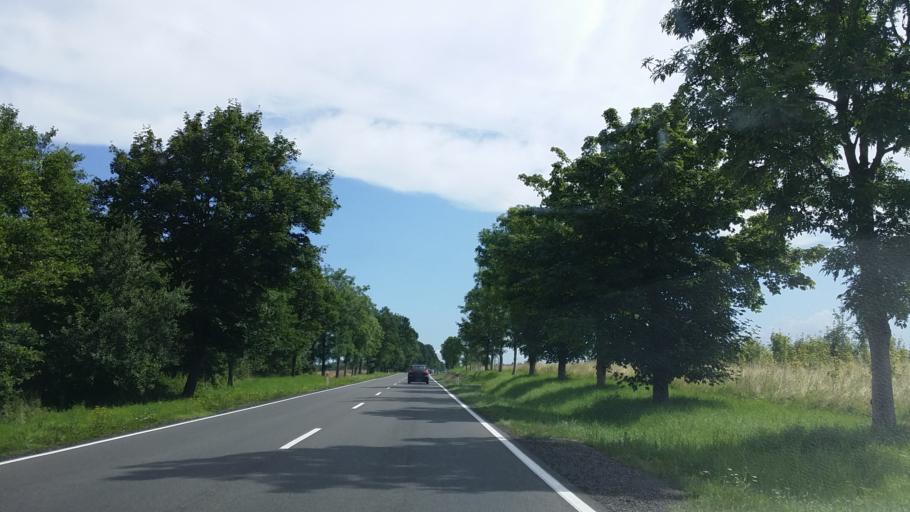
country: PL
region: West Pomeranian Voivodeship
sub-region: Powiat kolobrzeski
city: Ustronie Morskie
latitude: 54.1965
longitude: 15.7173
